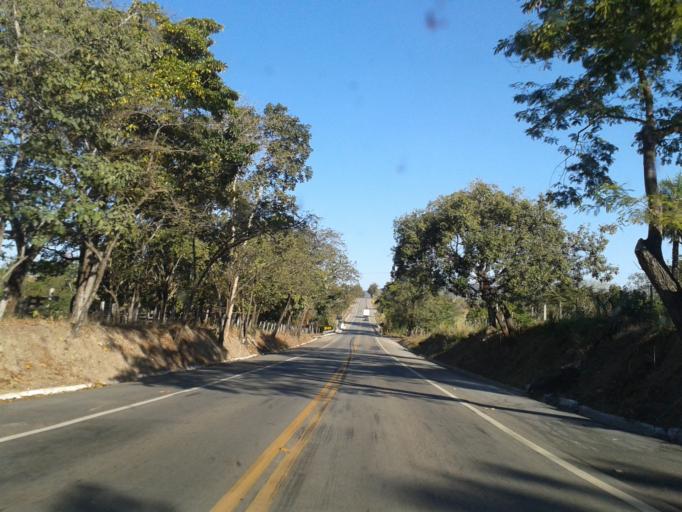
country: BR
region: Goias
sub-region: Itapuranga
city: Itapuranga
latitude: -15.4276
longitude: -50.3742
